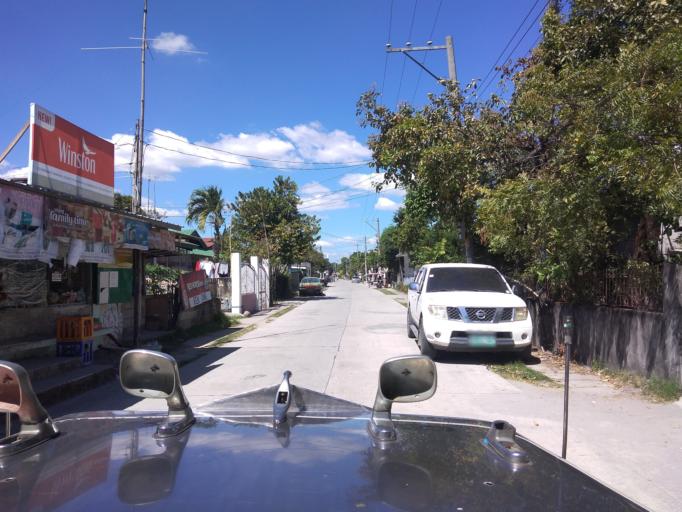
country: PH
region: Central Luzon
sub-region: Province of Pampanga
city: Magliman
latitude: 15.0328
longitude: 120.6492
